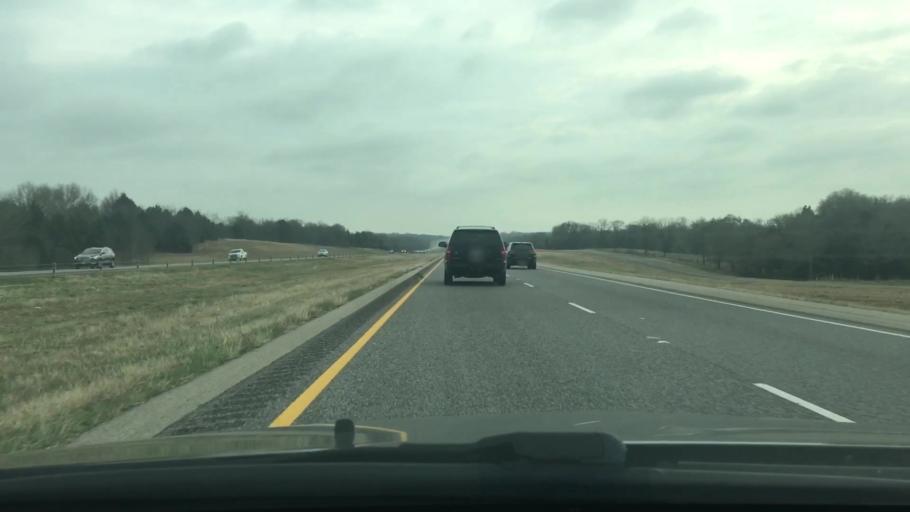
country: US
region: Texas
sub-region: Freestone County
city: Fairfield
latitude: 31.6635
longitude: -96.1623
